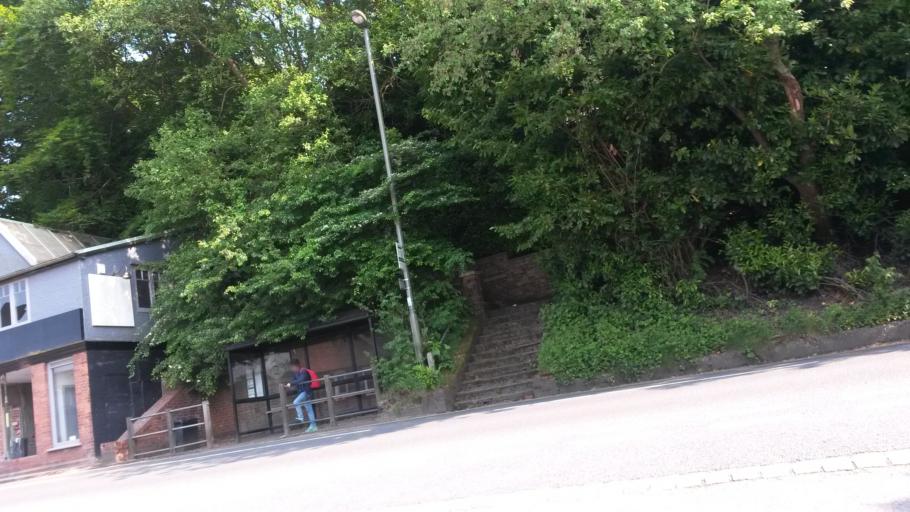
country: GB
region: England
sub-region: Surrey
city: Haslemere
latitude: 51.0887
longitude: -0.7188
